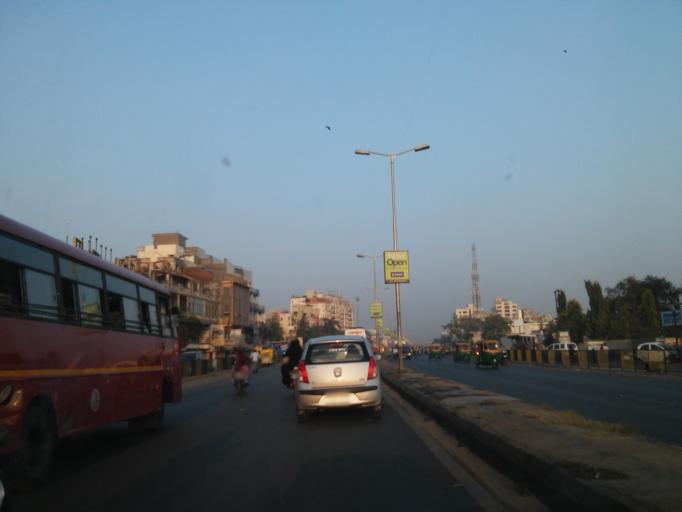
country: IN
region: Gujarat
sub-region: Ahmadabad
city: Sarkhej
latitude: 22.9922
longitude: 72.5209
